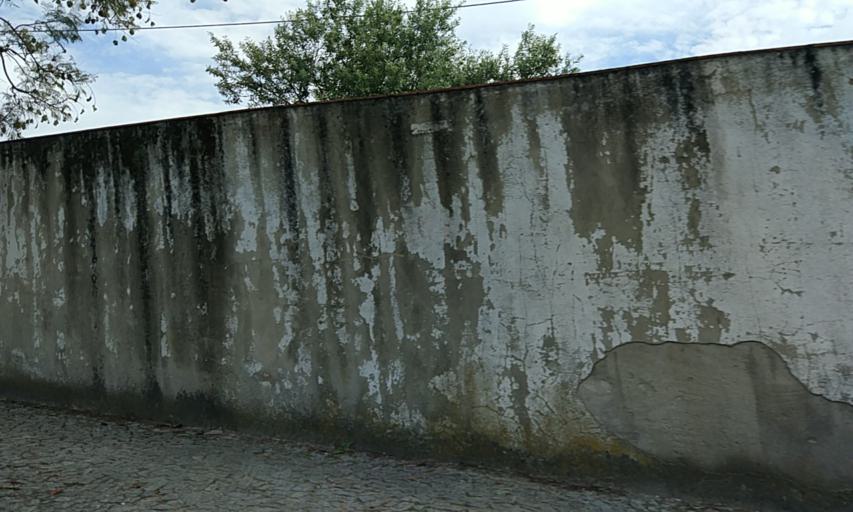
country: PT
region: Evora
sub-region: Evora
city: Evora
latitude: 38.5674
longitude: -7.9250
